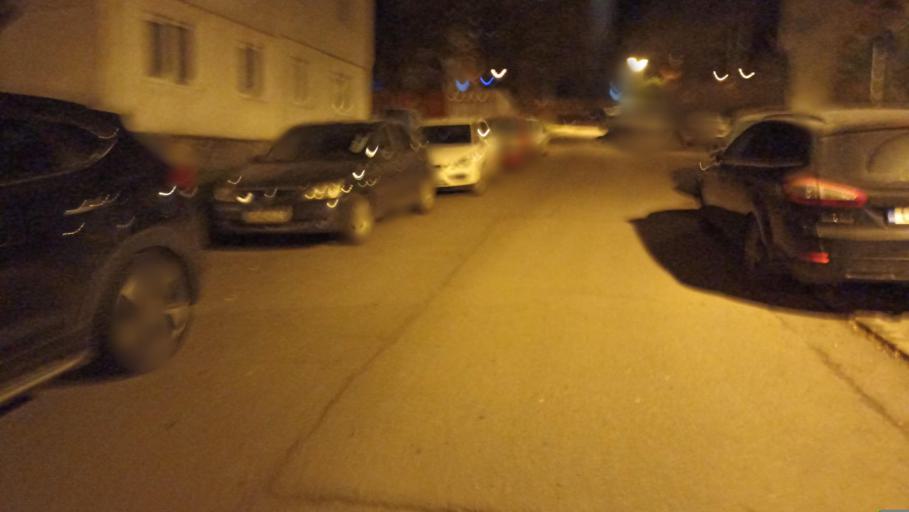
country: RO
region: Cluj
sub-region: Municipiul Cluj-Napoca
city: Cluj-Napoca
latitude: 46.7503
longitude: 23.5504
